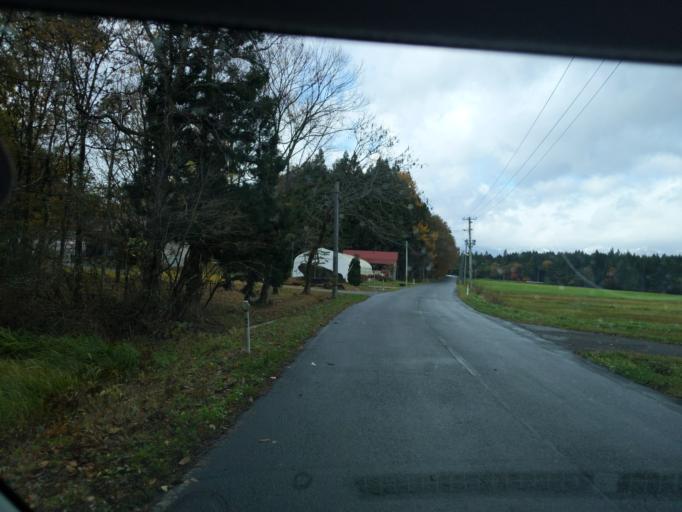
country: JP
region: Iwate
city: Mizusawa
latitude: 39.1033
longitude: 140.9917
